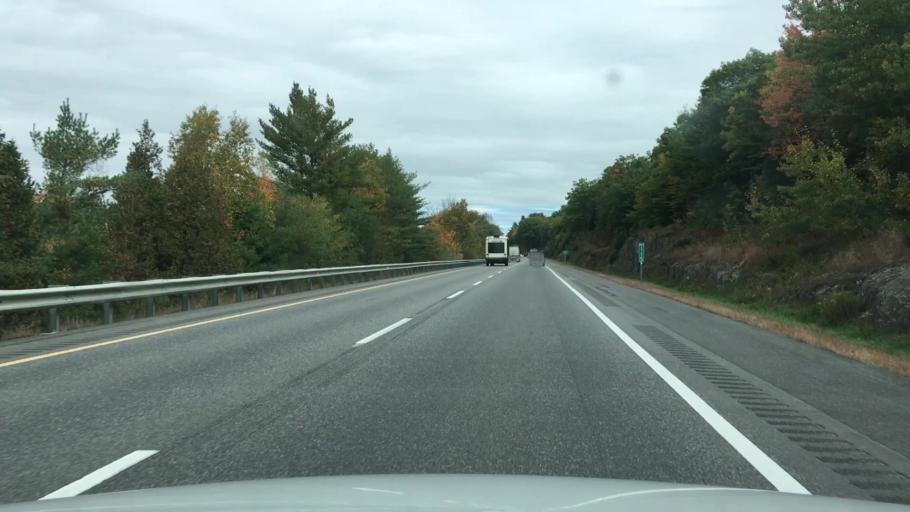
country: US
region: Maine
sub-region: Kennebec County
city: Sidney
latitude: 44.3814
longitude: -69.7663
